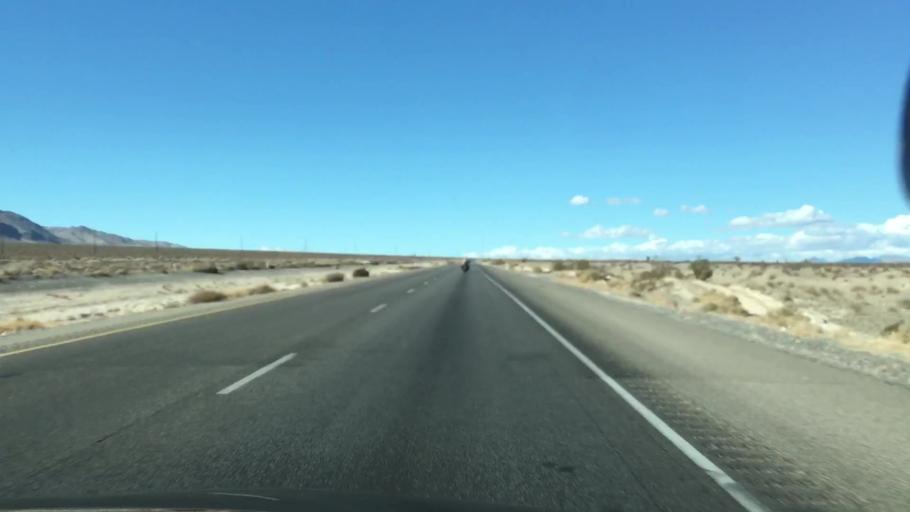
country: US
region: Nevada
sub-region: Clark County
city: Summerlin South
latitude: 36.4117
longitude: -115.4093
